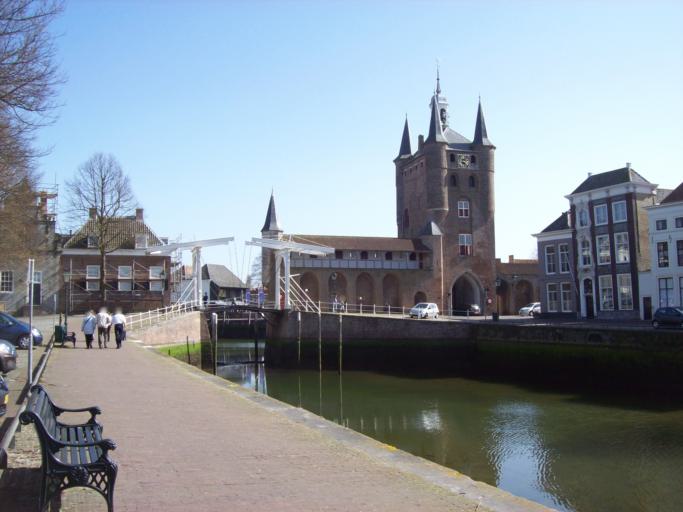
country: NL
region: Zeeland
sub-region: Schouwen-Duiveland
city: Scharendijke
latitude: 51.6481
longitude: 3.9255
